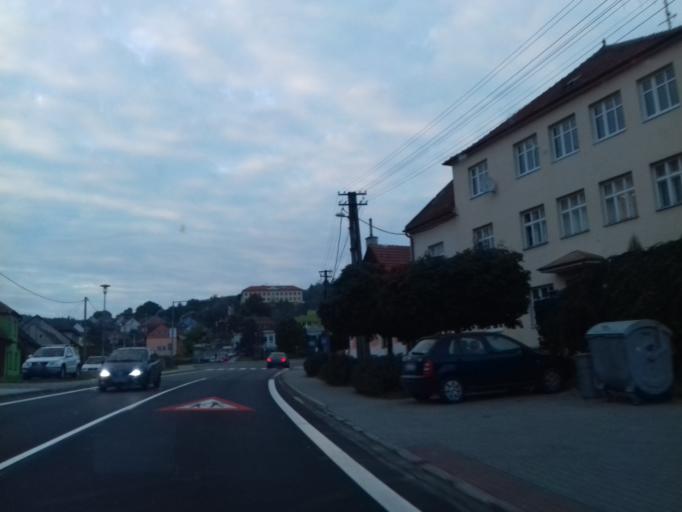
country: CZ
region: Zlin
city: Bojkovice
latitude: 48.9659
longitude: 17.8621
